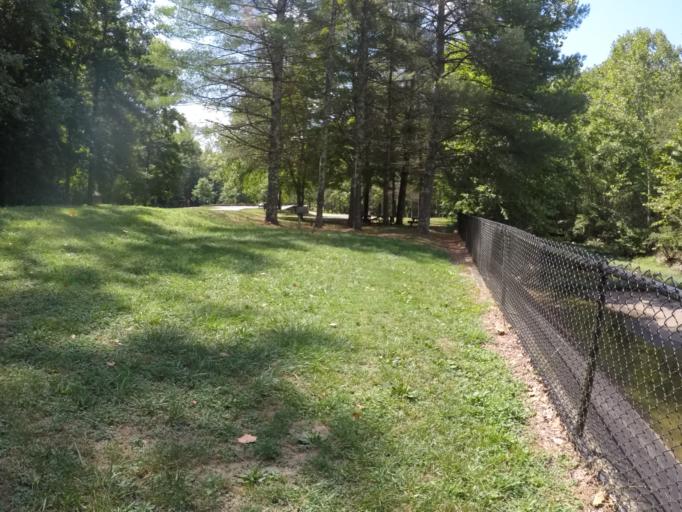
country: US
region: Ohio
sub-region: Lawrence County
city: Ironton
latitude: 38.6059
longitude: -82.6302
